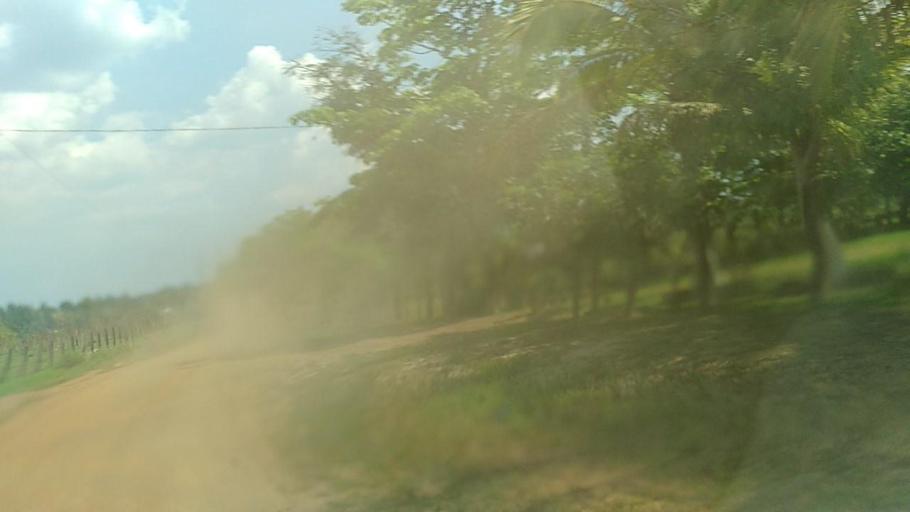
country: BR
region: Rondonia
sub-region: Porto Velho
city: Porto Velho
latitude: -8.6553
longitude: -64.1665
